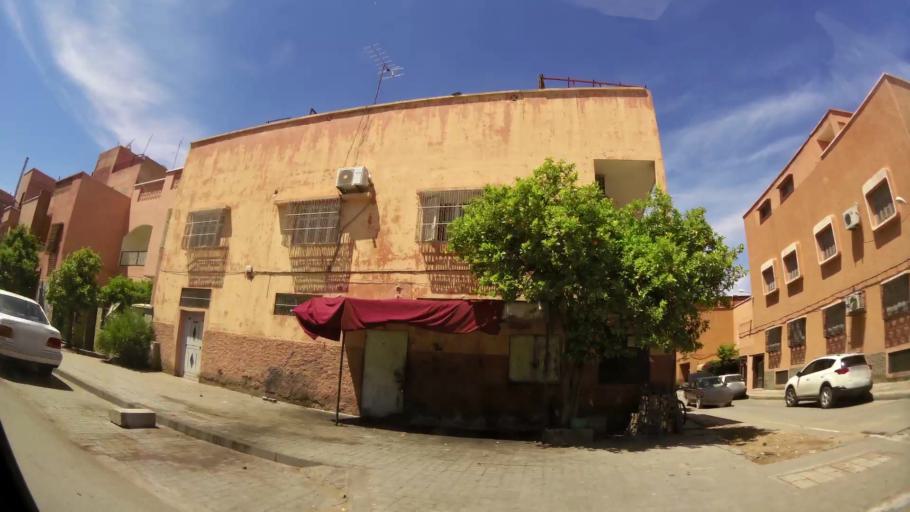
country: MA
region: Marrakech-Tensift-Al Haouz
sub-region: Marrakech
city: Marrakesh
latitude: 31.6548
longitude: -8.0021
